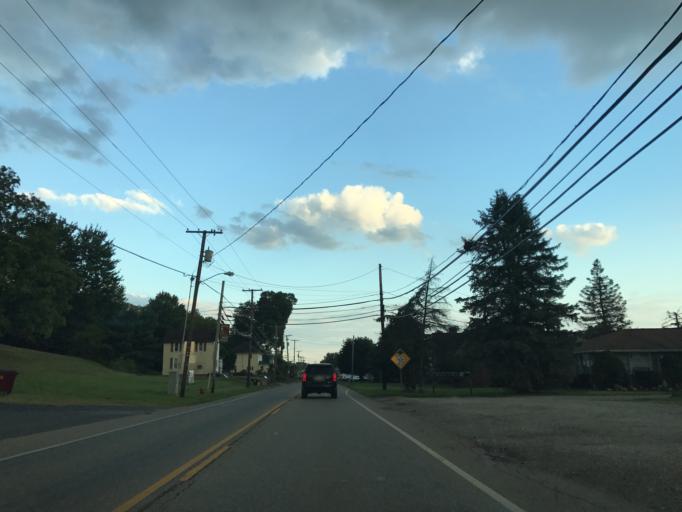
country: US
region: Ohio
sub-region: Stark County
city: Minerva
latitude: 40.7329
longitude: -81.1111
